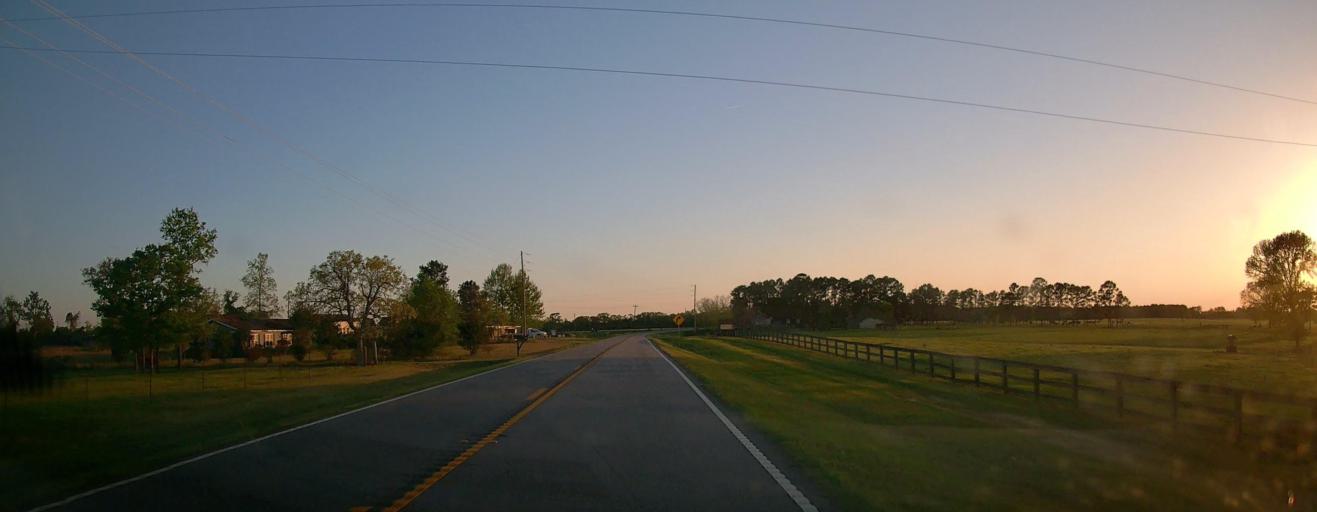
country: US
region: Georgia
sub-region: Marion County
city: Buena Vista
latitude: 32.4851
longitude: -84.6239
